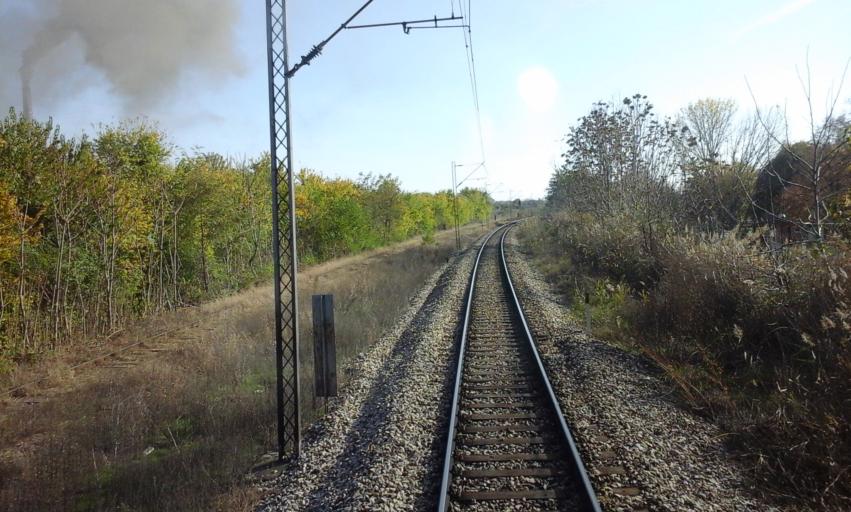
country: RS
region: Autonomna Pokrajina Vojvodina
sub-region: Severnobacki Okrug
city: Subotica
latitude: 46.0905
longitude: 19.6846
